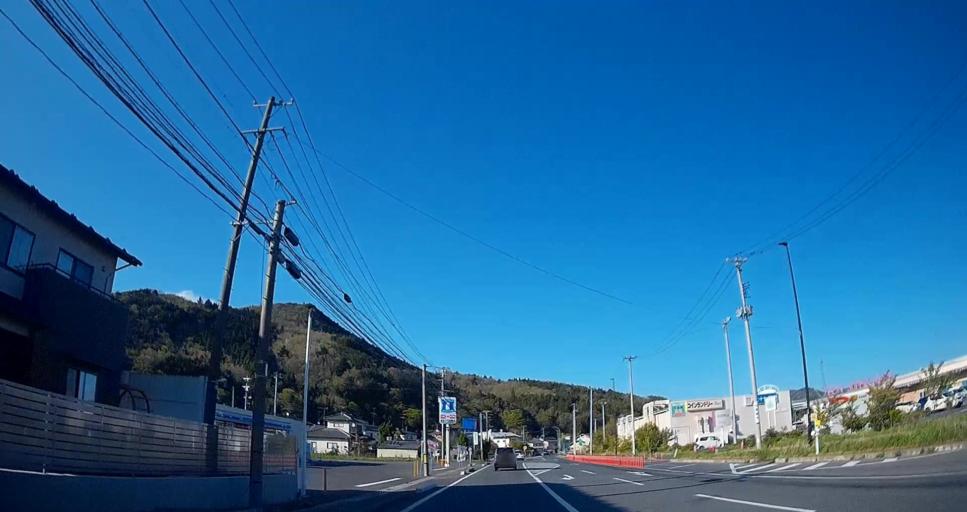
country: JP
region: Miyagi
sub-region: Oshika Gun
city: Onagawa Cho
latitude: 38.4280
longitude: 141.3738
